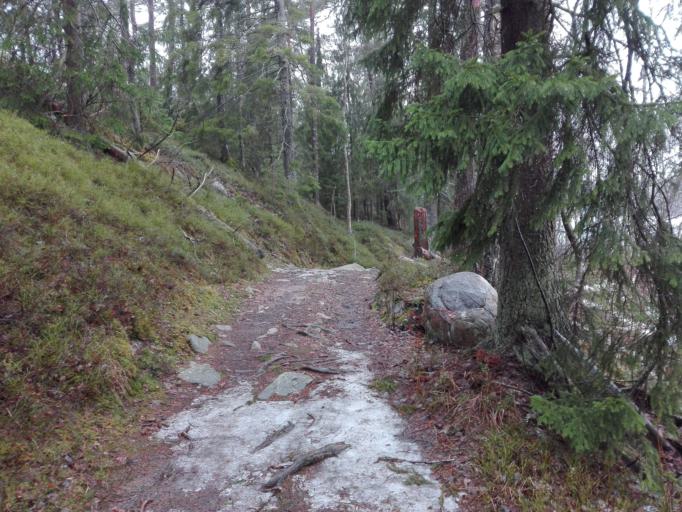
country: SE
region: Stockholm
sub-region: Nacka Kommun
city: Fisksatra
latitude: 59.2759
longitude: 18.2567
